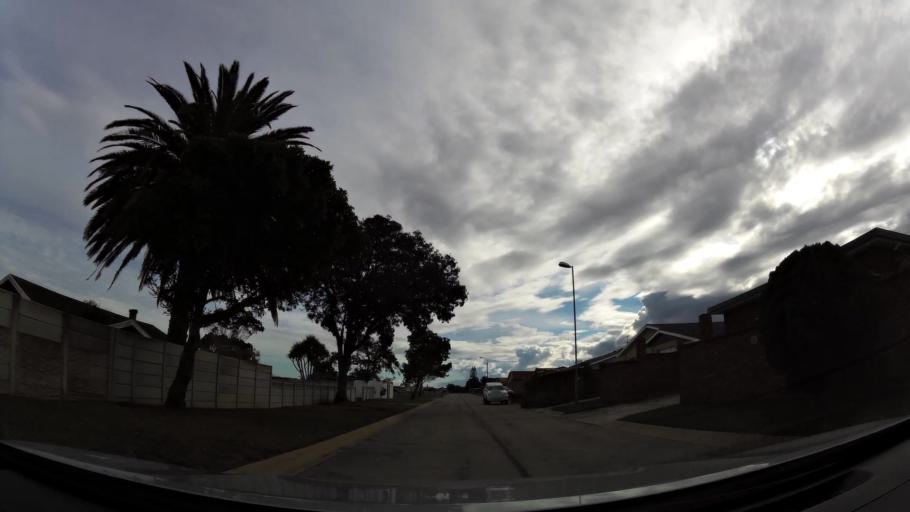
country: ZA
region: Eastern Cape
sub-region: Nelson Mandela Bay Metropolitan Municipality
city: Port Elizabeth
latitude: -33.9433
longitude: 25.4890
